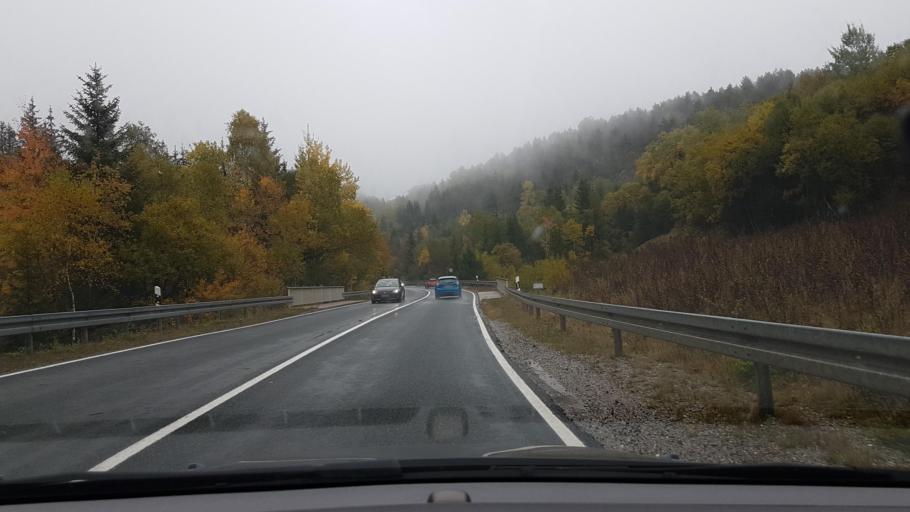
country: DE
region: Lower Saxony
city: Wildemann
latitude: 51.8024
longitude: 10.2990
